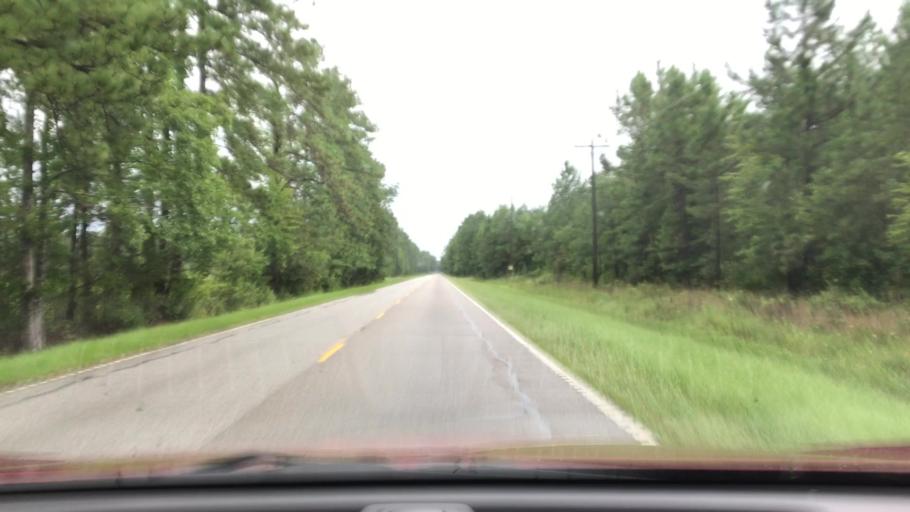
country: US
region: South Carolina
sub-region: Georgetown County
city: Murrells Inlet
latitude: 33.6018
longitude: -79.2002
